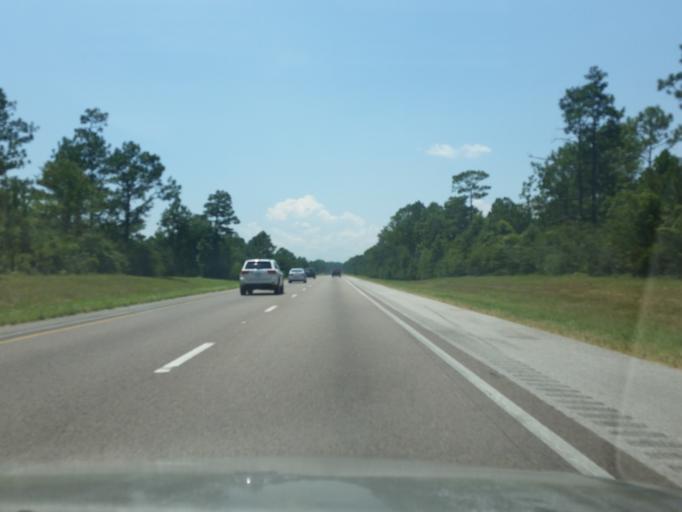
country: US
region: Florida
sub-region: Escambia County
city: Cantonment
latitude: 30.5785
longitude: -87.4473
